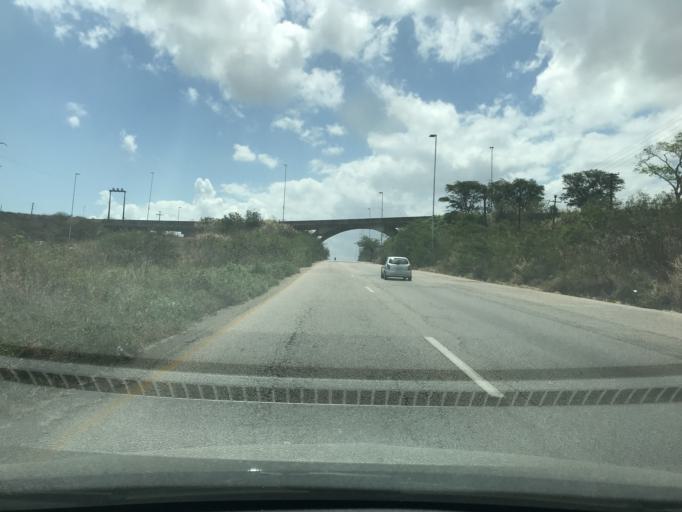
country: BR
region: Pernambuco
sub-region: Caruaru
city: Caruaru
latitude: -8.3062
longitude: -35.9636
